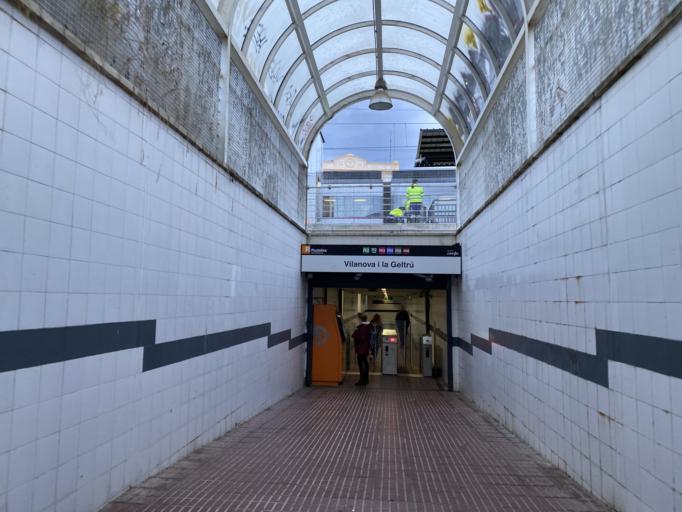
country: ES
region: Catalonia
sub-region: Provincia de Barcelona
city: Vilanova i la Geltru
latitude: 41.2197
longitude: 1.7314
